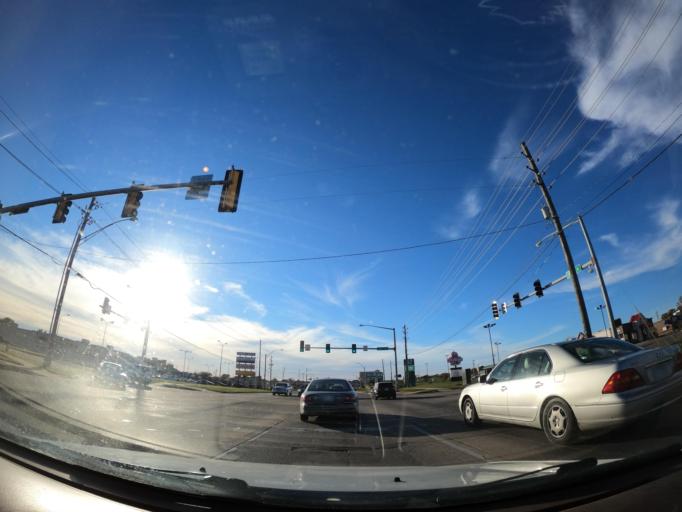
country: US
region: Oklahoma
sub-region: Tulsa County
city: Owasso
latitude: 36.2786
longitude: -95.8434
